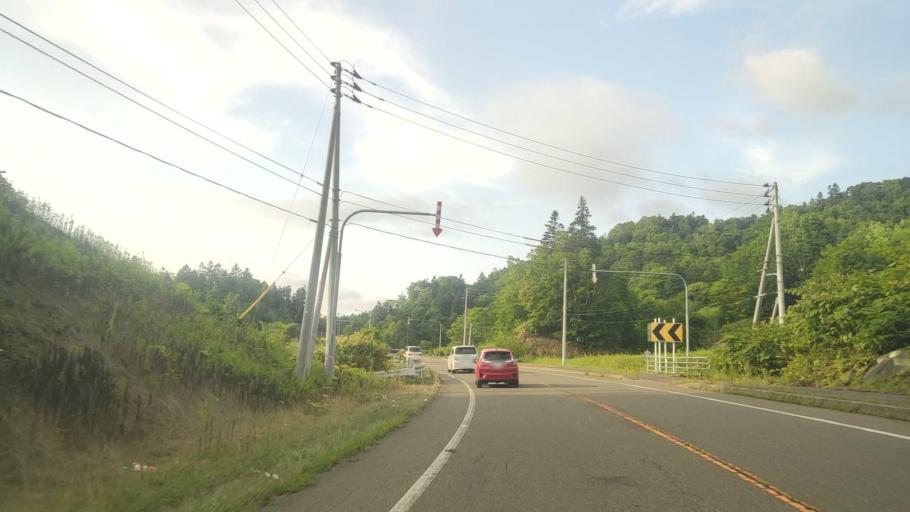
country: JP
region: Hokkaido
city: Iwamizawa
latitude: 43.0238
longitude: 141.9544
